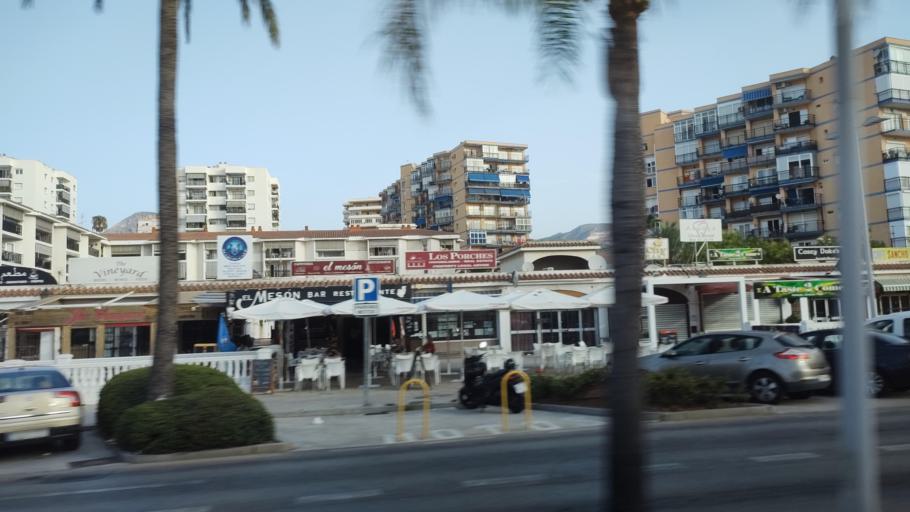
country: ES
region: Andalusia
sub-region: Provincia de Malaga
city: Torremolinos
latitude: 36.6006
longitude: -4.5158
